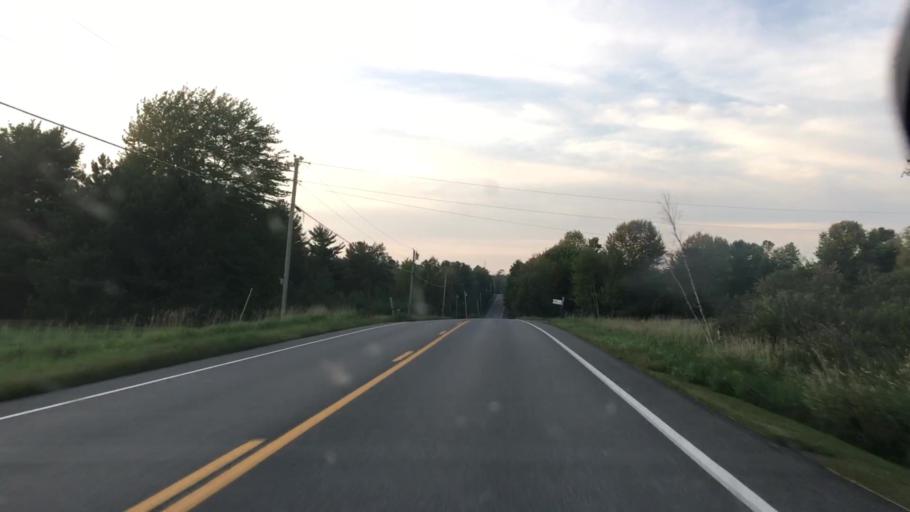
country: US
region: Maine
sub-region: Penobscot County
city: Hermon
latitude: 44.7480
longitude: -68.9683
